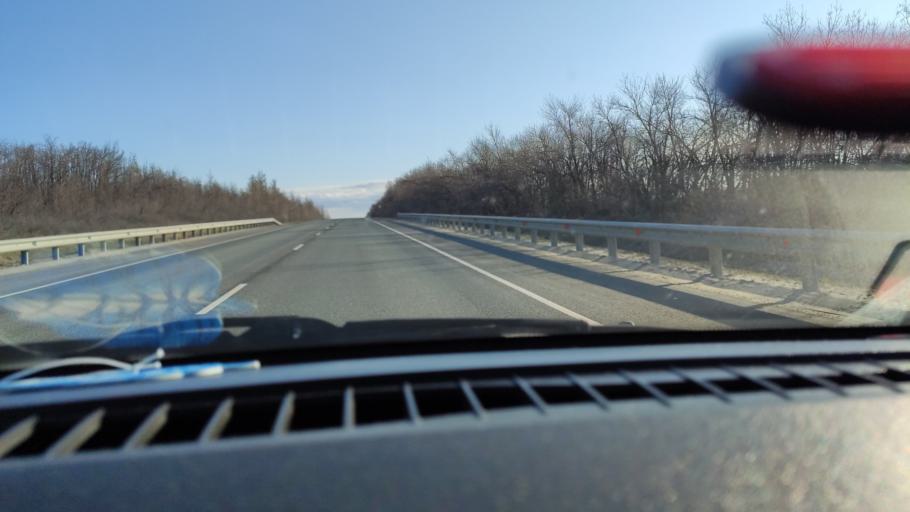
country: RU
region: Saratov
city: Dukhovnitskoye
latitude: 52.6208
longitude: 48.1728
